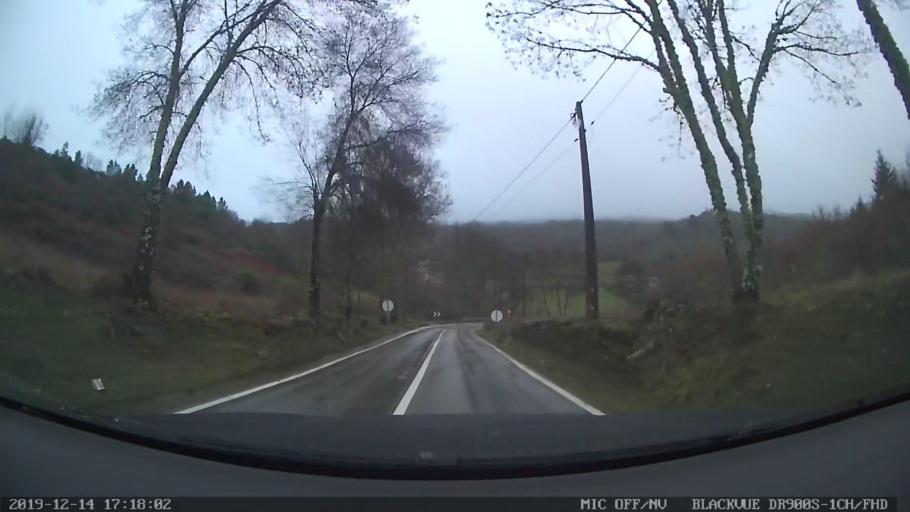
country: PT
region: Vila Real
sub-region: Vila Pouca de Aguiar
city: Vila Pouca de Aguiar
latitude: 41.4963
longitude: -7.6372
